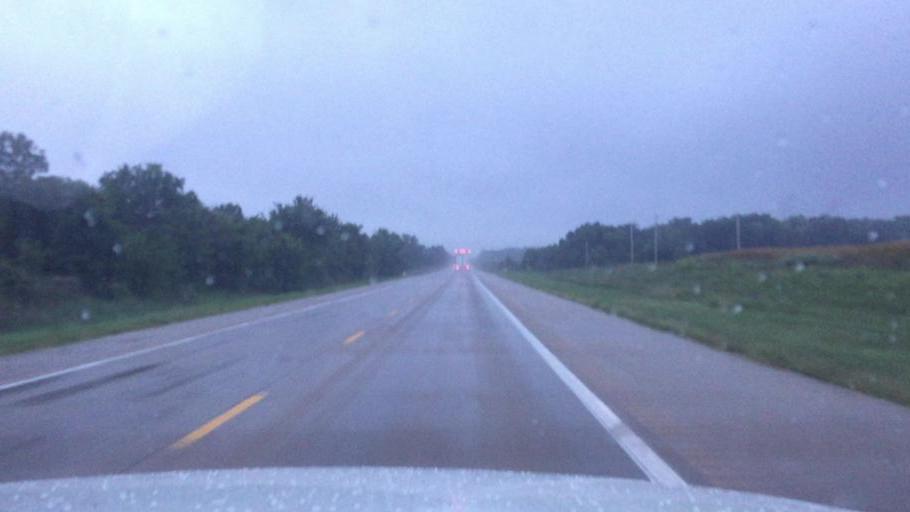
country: US
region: Kansas
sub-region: Neosho County
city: Chanute
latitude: 37.5596
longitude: -95.4709
